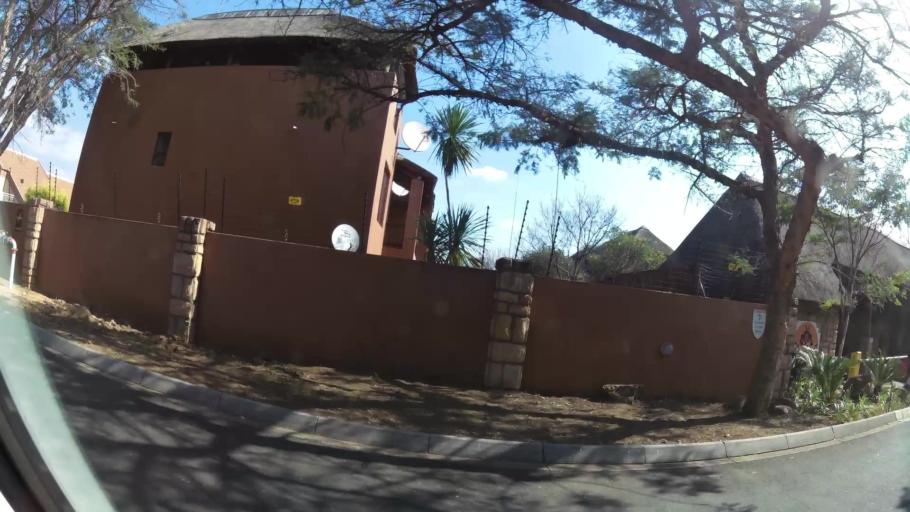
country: ZA
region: Gauteng
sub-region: City of Johannesburg Metropolitan Municipality
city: Midrand
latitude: -26.0278
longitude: 28.0649
